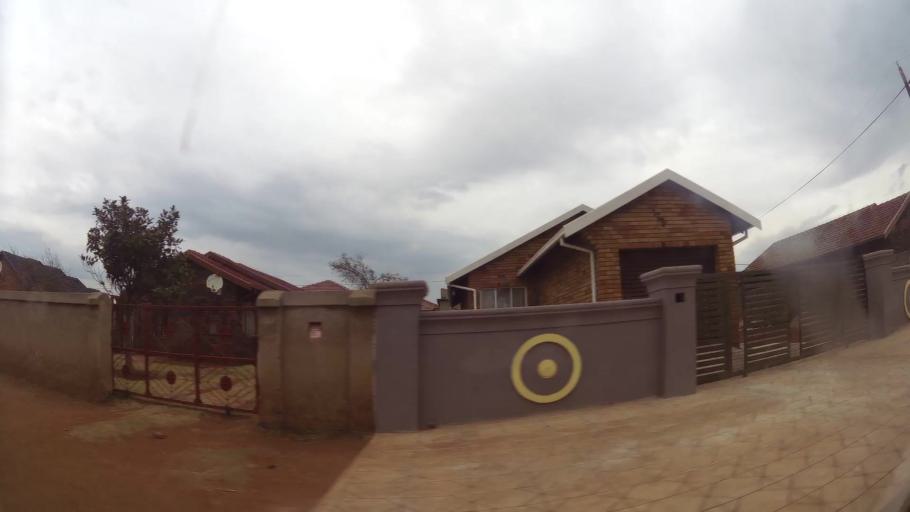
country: ZA
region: Gauteng
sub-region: Ekurhuleni Metropolitan Municipality
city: Germiston
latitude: -26.3799
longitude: 28.1574
